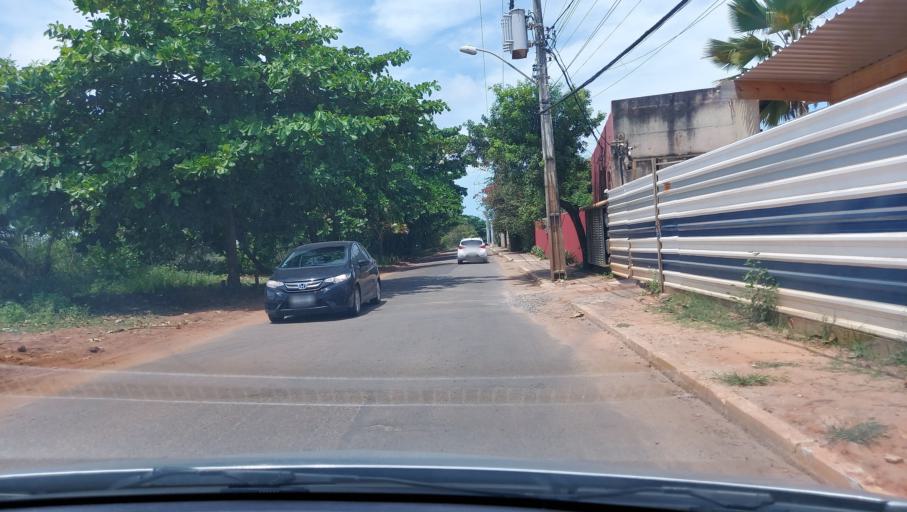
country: BR
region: Bahia
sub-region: Mata De Sao Joao
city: Mata de Sao Joao
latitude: -12.6116
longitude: -38.0435
